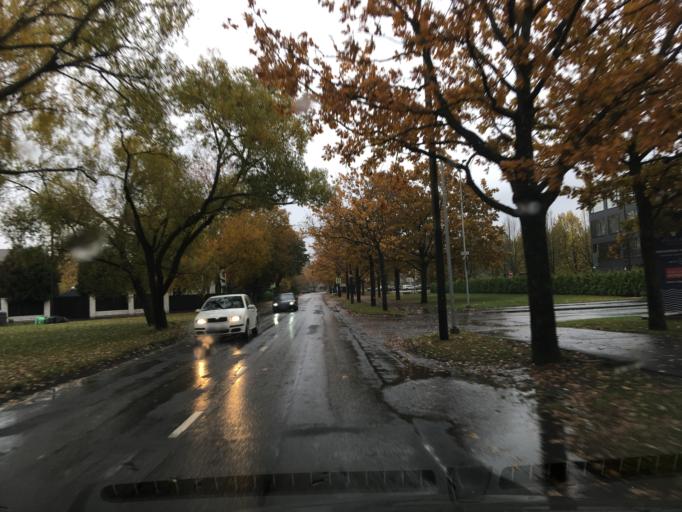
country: EE
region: Paernumaa
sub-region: Paernu linn
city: Parnu
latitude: 58.3740
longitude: 24.5224
